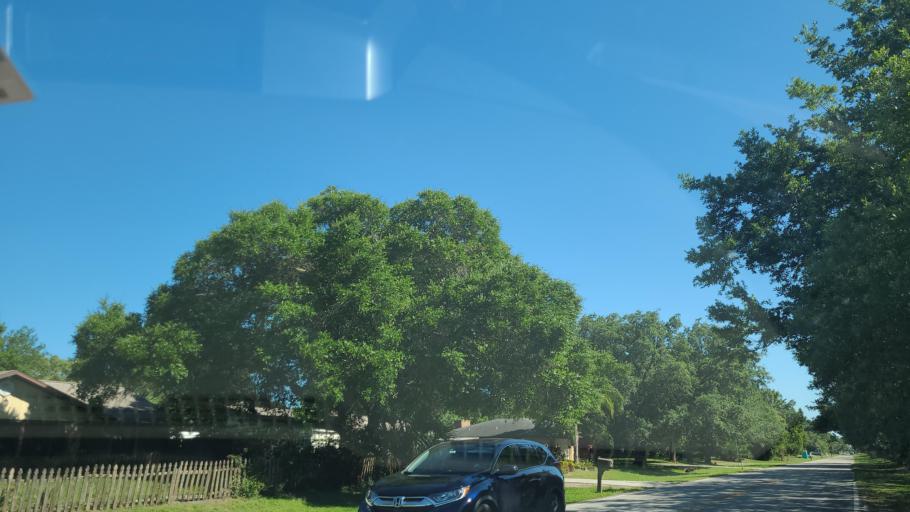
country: US
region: Florida
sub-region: Indian River County
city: Sebastian
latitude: 27.7817
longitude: -80.4946
